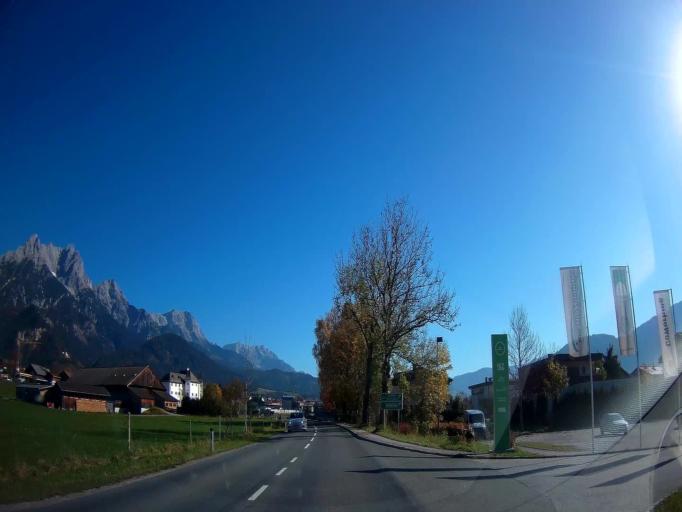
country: AT
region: Salzburg
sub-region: Politischer Bezirk Zell am See
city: Saalfelden am Steinernen Meer
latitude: 47.4309
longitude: 12.8321
